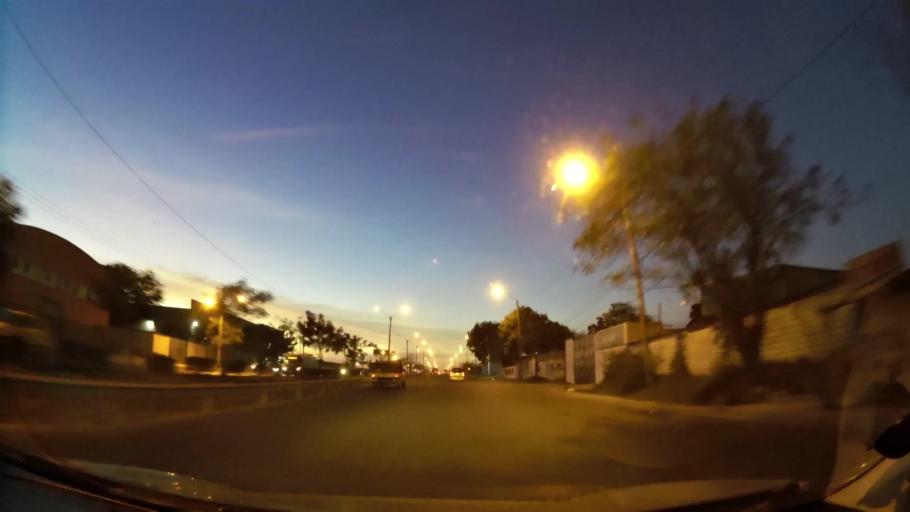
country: CO
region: Atlantico
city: Barranquilla
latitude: 10.9275
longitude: -74.8265
